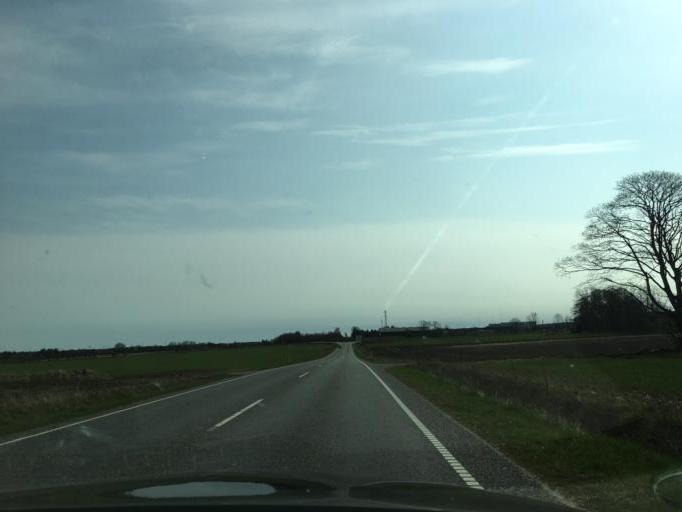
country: DK
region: South Denmark
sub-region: Vejen Kommune
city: Vejen
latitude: 55.4915
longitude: 9.0962
